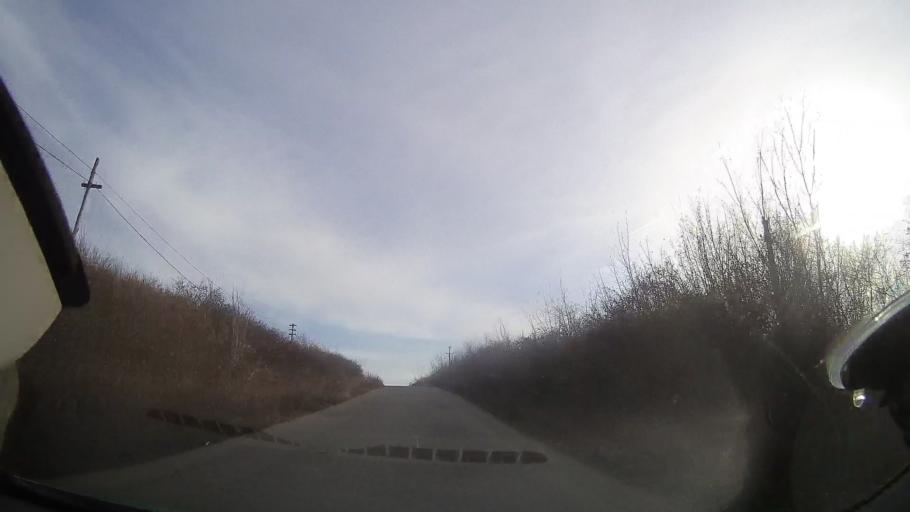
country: RO
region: Bihor
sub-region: Comuna Sarbi
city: Sarbi
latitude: 47.1864
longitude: 22.1284
